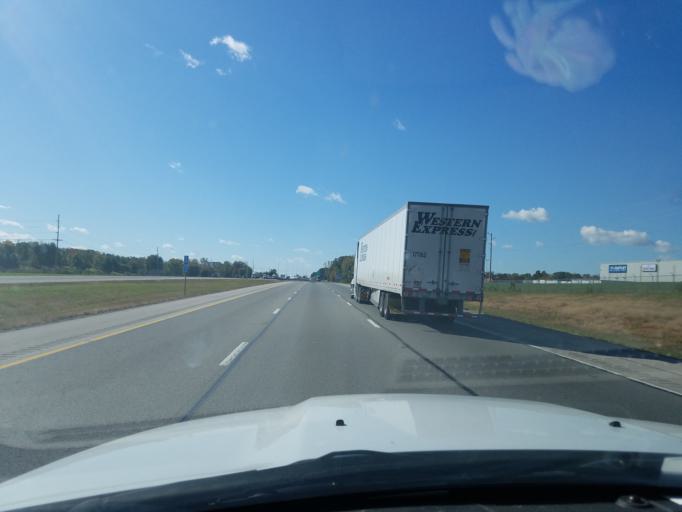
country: US
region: Kentucky
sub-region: Warren County
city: Bowling Green
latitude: 36.9556
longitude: -86.4048
